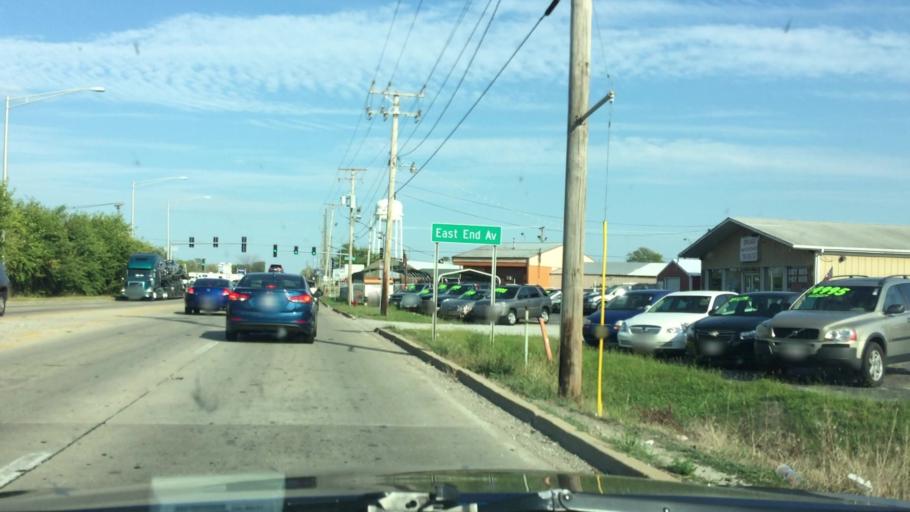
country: US
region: Illinois
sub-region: Cook County
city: South Chicago Heights
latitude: 41.4811
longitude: -87.6347
